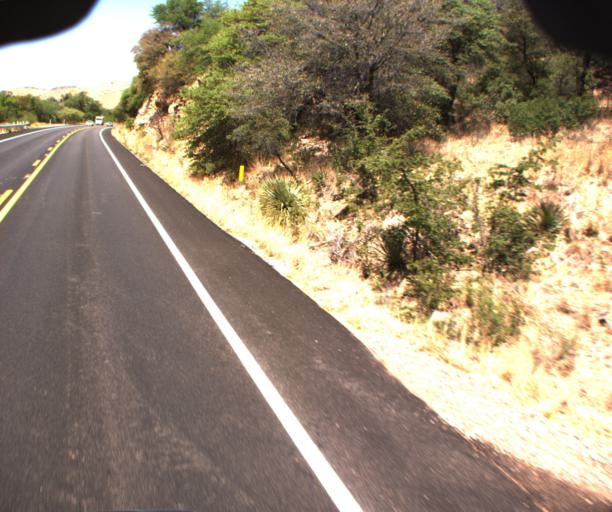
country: US
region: Arizona
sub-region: Cochise County
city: Bisbee
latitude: 31.4879
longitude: -109.9874
